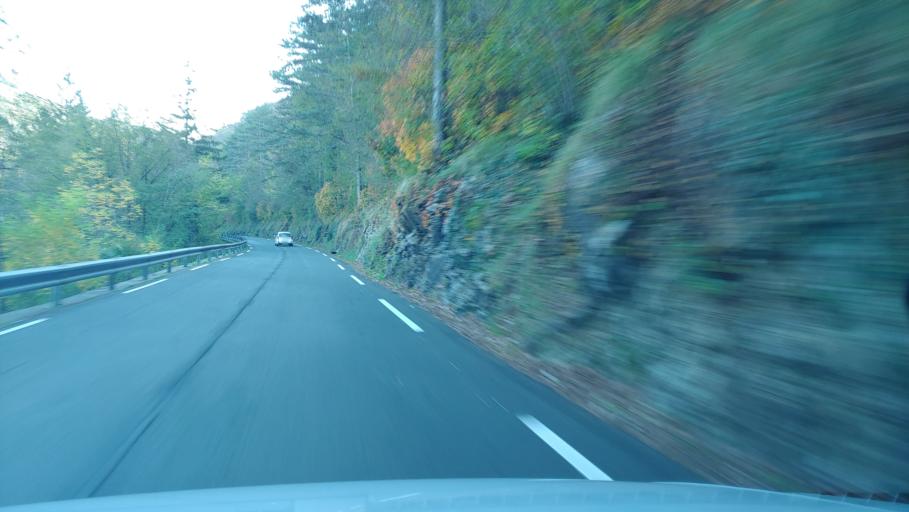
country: SI
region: Ajdovscina
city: Ajdovscina
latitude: 45.8049
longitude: 13.8608
